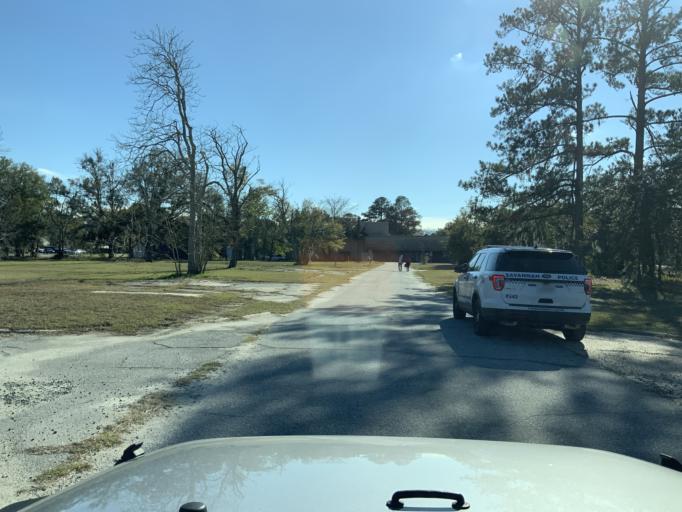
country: US
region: Georgia
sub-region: Chatham County
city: Thunderbolt
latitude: 32.0585
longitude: -81.0600
